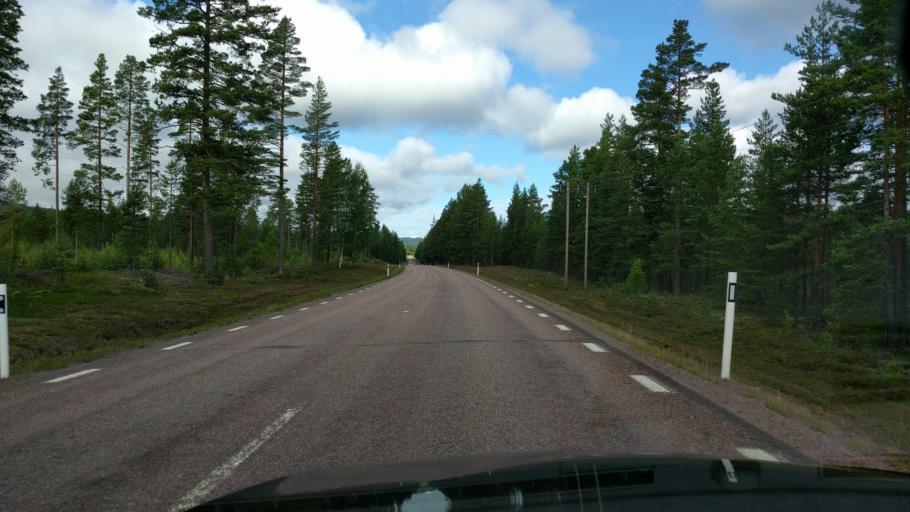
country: SE
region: Dalarna
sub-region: Mora Kommun
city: Mora
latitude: 61.0703
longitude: 14.3791
